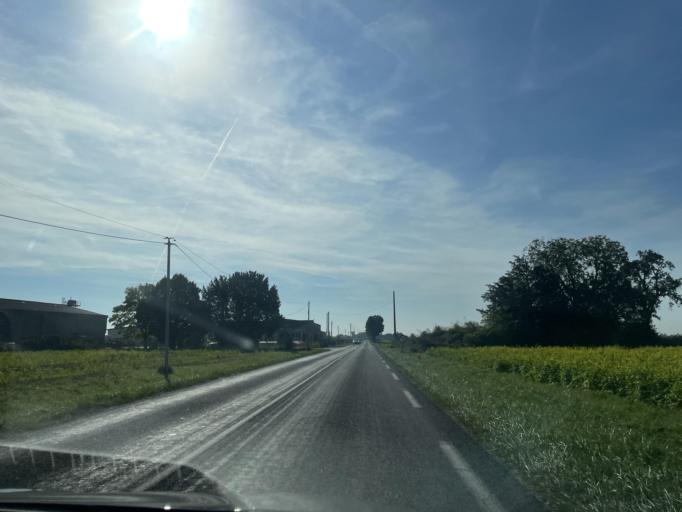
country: FR
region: Ile-de-France
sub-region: Departement de Seine-et-Marne
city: Coulommiers
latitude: 48.8588
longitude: 3.0909
